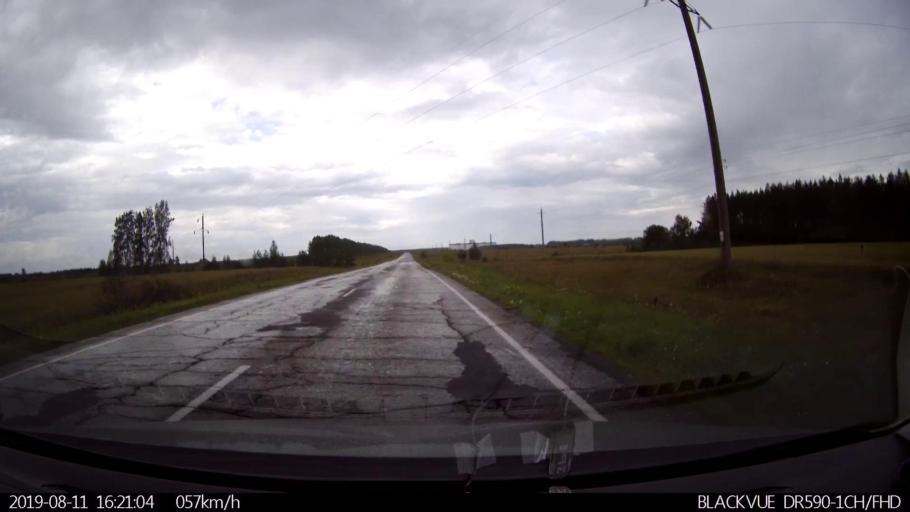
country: RU
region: Ulyanovsk
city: Mayna
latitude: 54.0769
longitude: 47.5998
